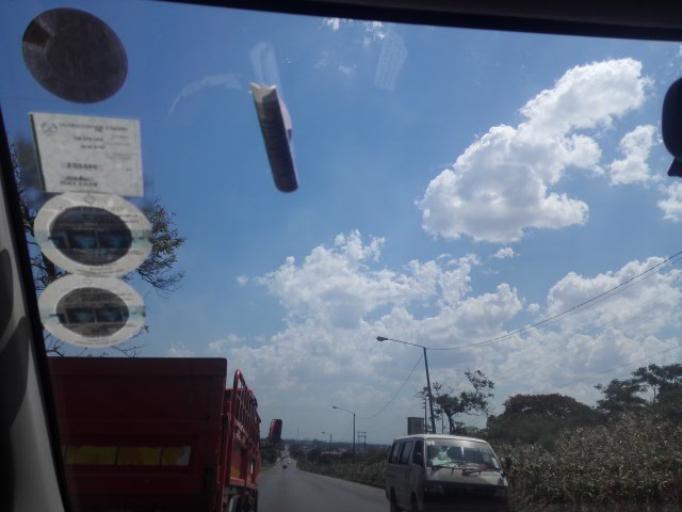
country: MZ
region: Maputo
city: Matola
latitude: -25.9633
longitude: 32.4474
